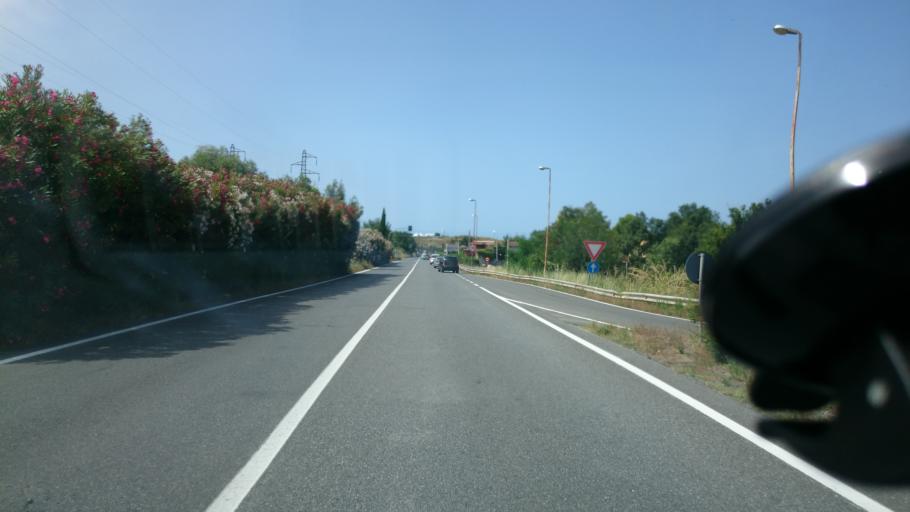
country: IT
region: Calabria
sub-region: Provincia di Cosenza
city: San Nicola Arcella
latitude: 39.8409
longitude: 15.7955
